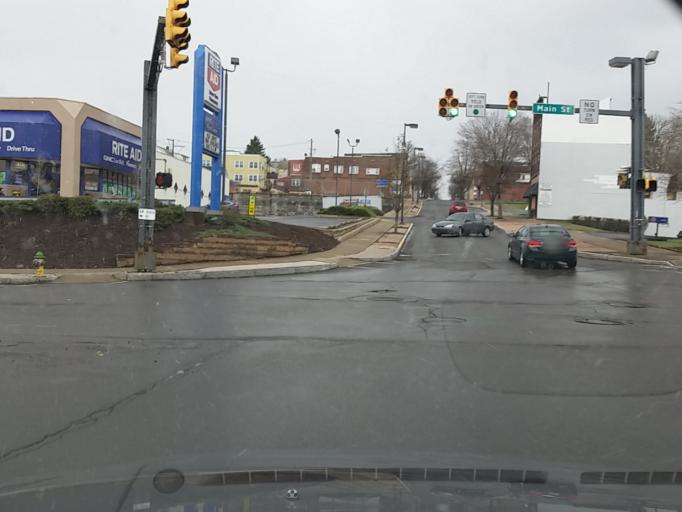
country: US
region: Pennsylvania
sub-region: Luzerne County
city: Nanticoke
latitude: 41.2053
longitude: -76.0051
